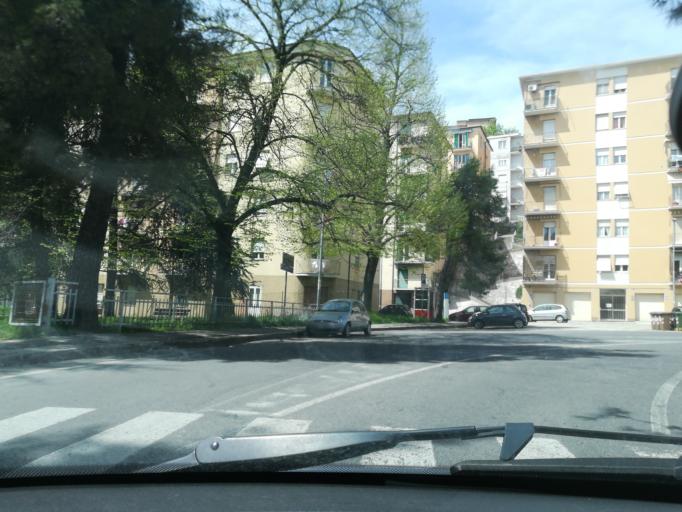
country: IT
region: The Marches
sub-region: Provincia di Macerata
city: Macerata
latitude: 43.2961
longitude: 13.4504
